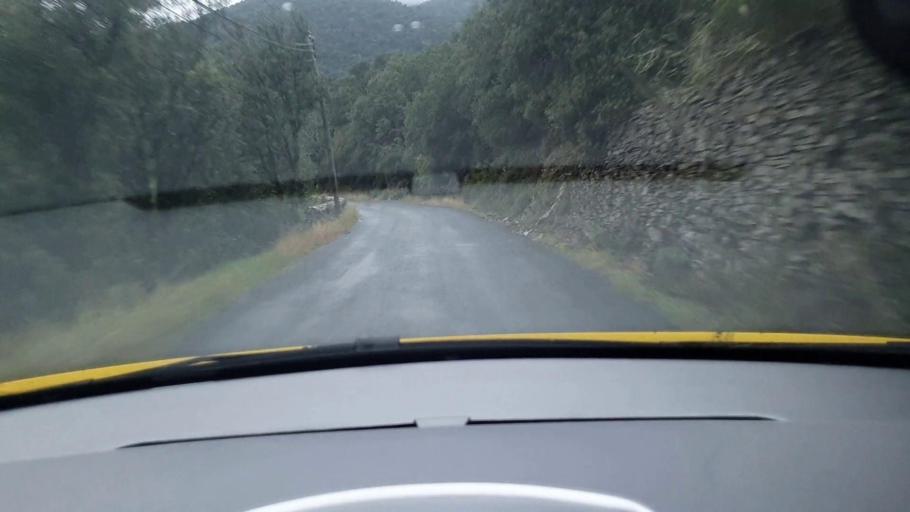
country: FR
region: Languedoc-Roussillon
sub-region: Departement du Gard
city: Sumene
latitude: 44.0127
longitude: 3.7192
